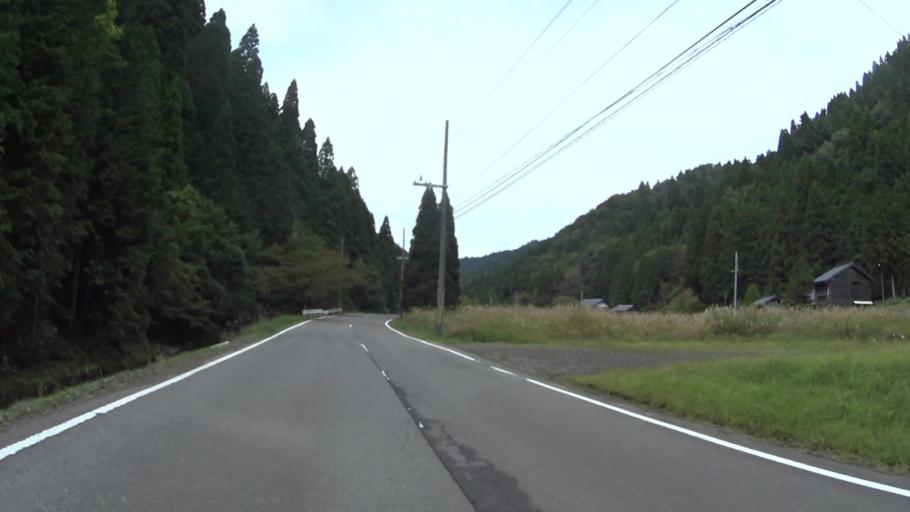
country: JP
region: Shiga Prefecture
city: Kitahama
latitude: 35.2621
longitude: 135.7504
